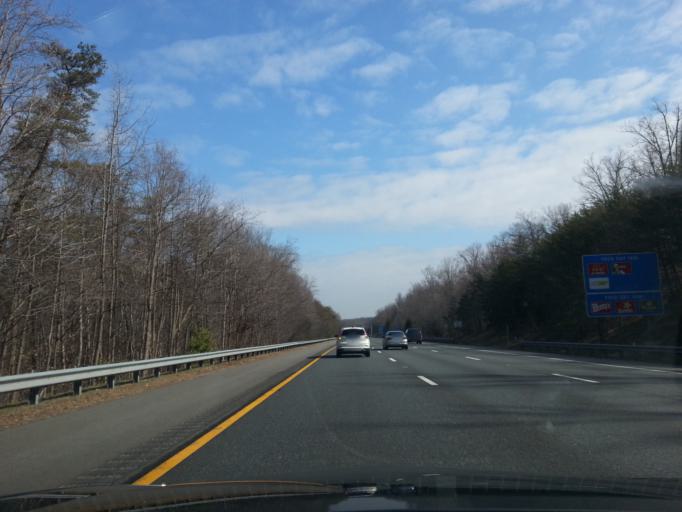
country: US
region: Virginia
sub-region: Stafford County
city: Stafford
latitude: 38.4362
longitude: -77.4130
